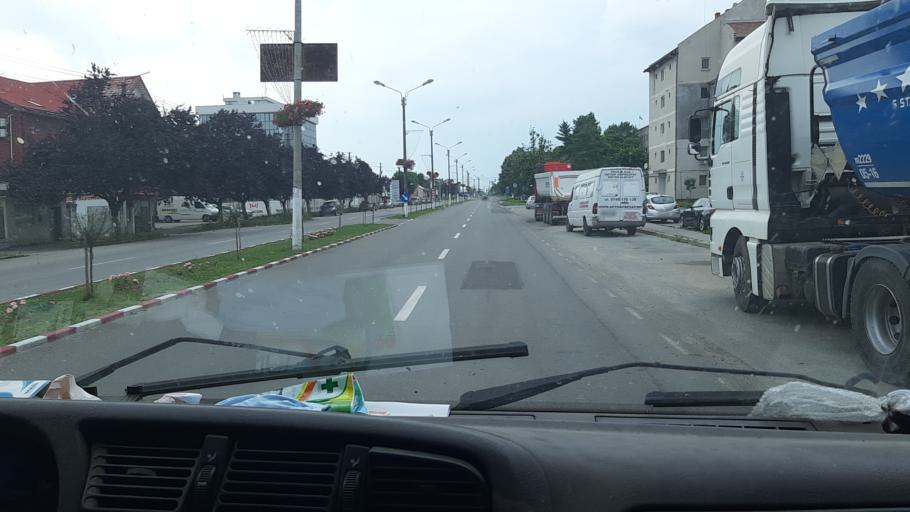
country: RO
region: Timis
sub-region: Municipiul Lugoj
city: Lugoj
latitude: 45.6984
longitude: 21.8963
